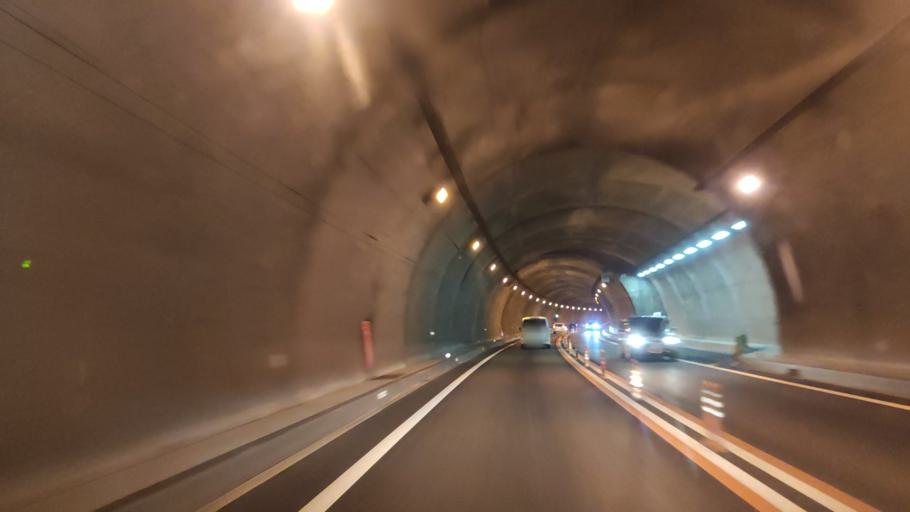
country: JP
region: Ehime
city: Kawanoecho
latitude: 33.9967
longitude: 133.6388
